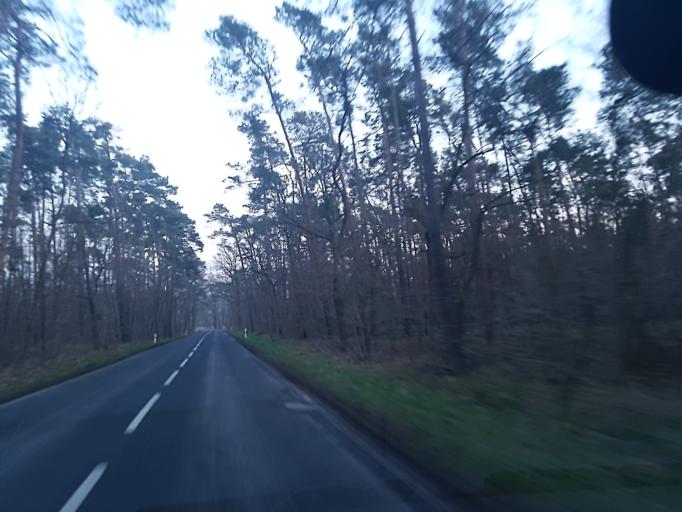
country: DE
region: Saxony-Anhalt
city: Holzdorf
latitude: 51.7761
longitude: 13.0786
